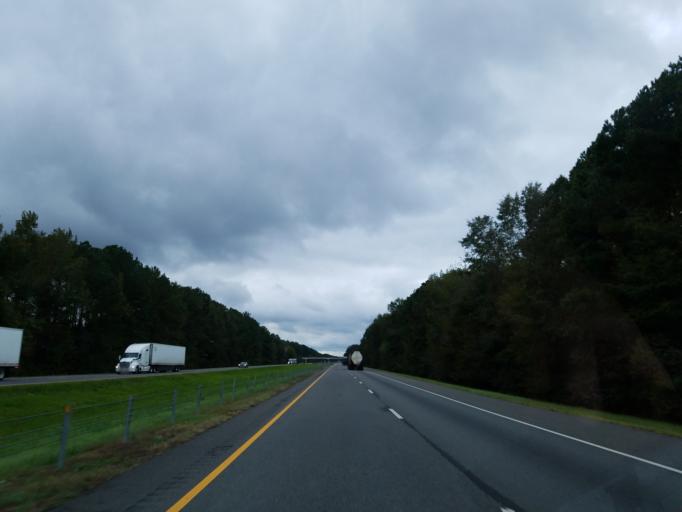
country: US
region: Alabama
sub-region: Greene County
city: Eutaw
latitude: 32.7653
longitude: -88.0666
